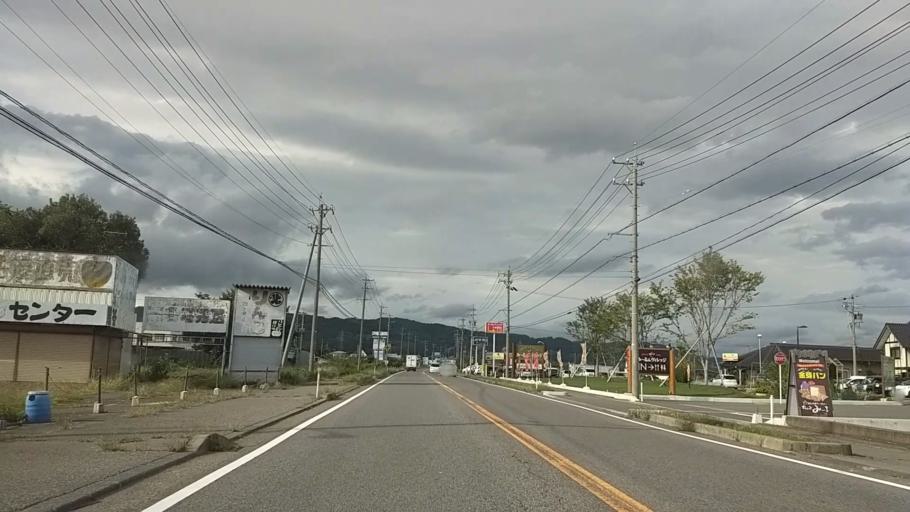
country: JP
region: Nagano
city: Suzaka
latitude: 36.6882
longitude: 138.2681
